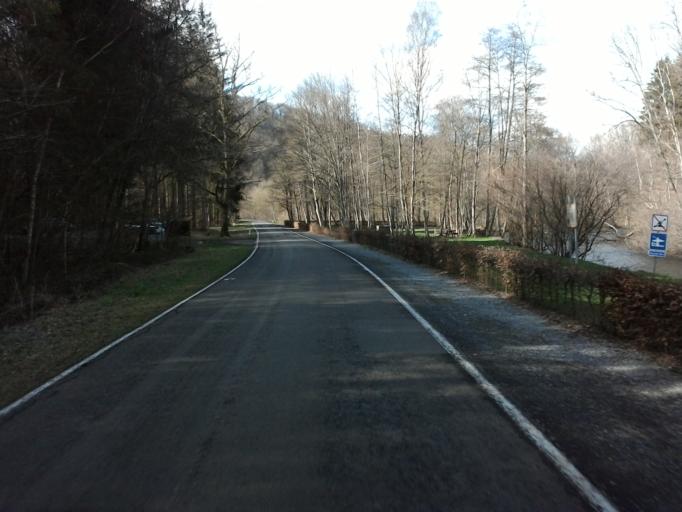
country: BE
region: Wallonia
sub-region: Province du Luxembourg
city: Daverdisse
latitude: 50.0438
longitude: 5.1372
